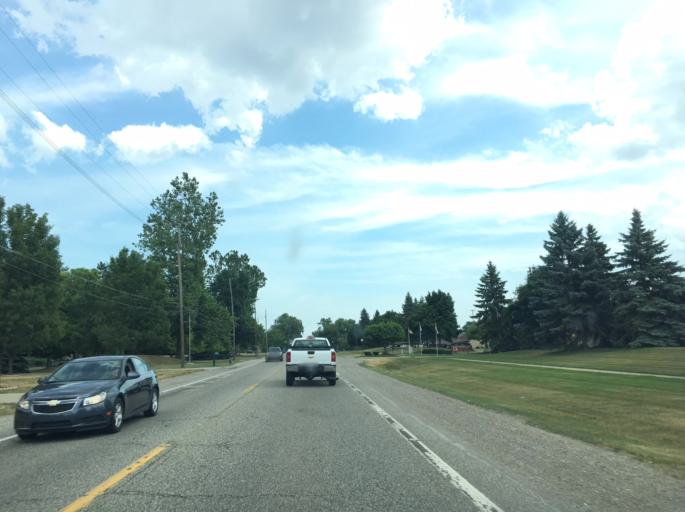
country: US
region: Michigan
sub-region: Macomb County
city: Utica
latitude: 42.6051
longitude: -83.0258
